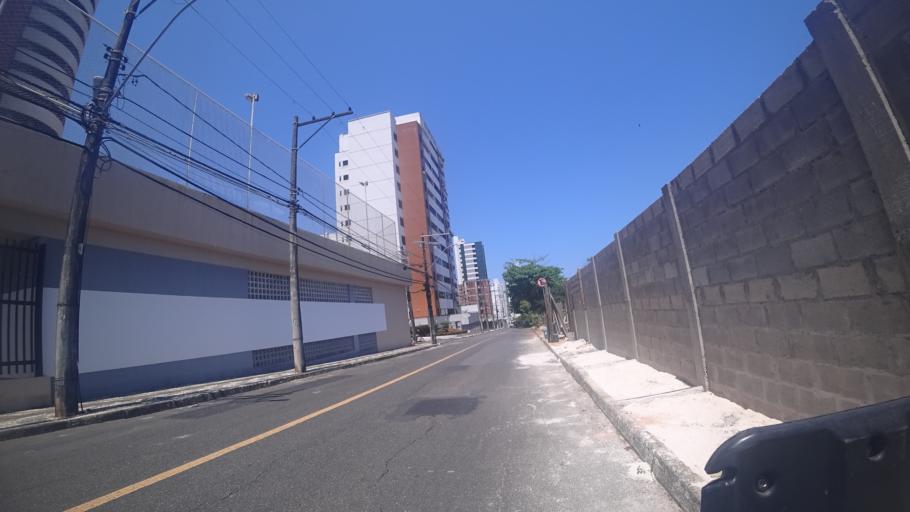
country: BR
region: Bahia
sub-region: Salvador
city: Salvador
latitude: -12.9879
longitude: -38.4603
